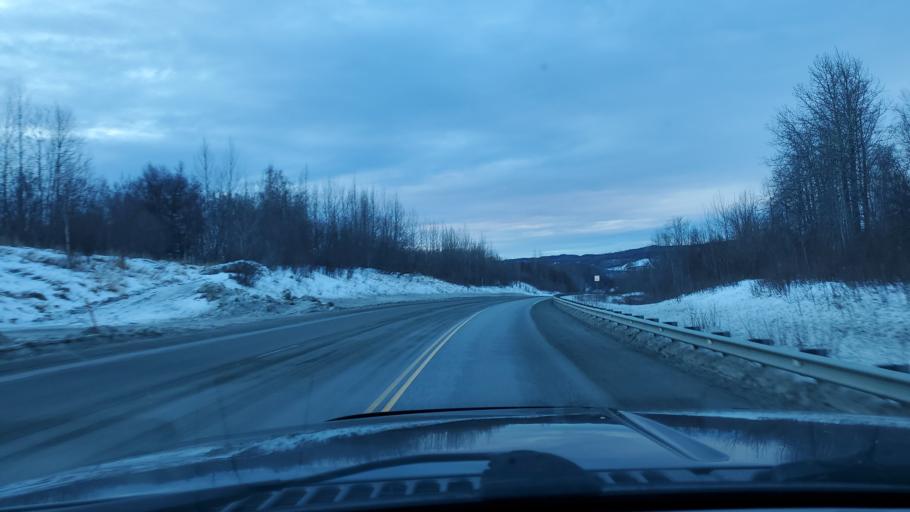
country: US
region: Alaska
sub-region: Matanuska-Susitna Borough
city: Lazy Mountain
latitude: 61.6778
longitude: -148.9969
